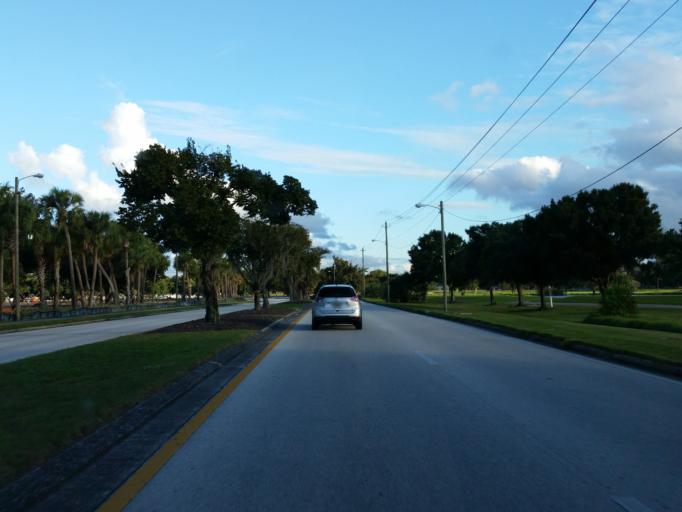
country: US
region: Florida
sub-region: Hillsborough County
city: Town 'n' Country
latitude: 27.9791
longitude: -82.5545
